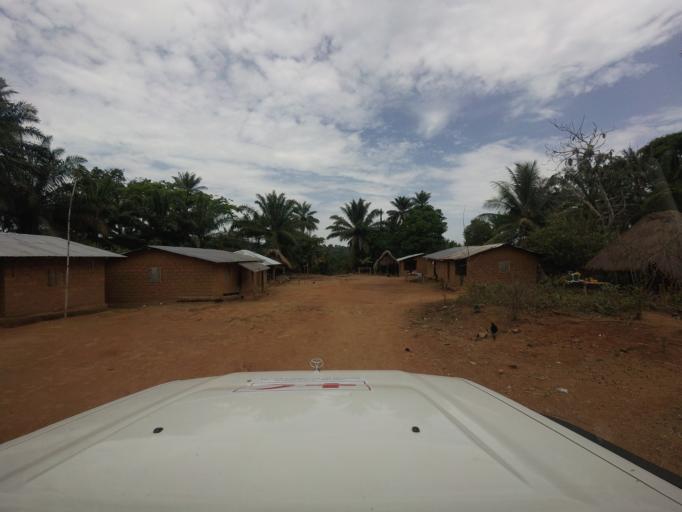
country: SL
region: Eastern Province
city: Buedu
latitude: 8.2476
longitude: -10.2529
